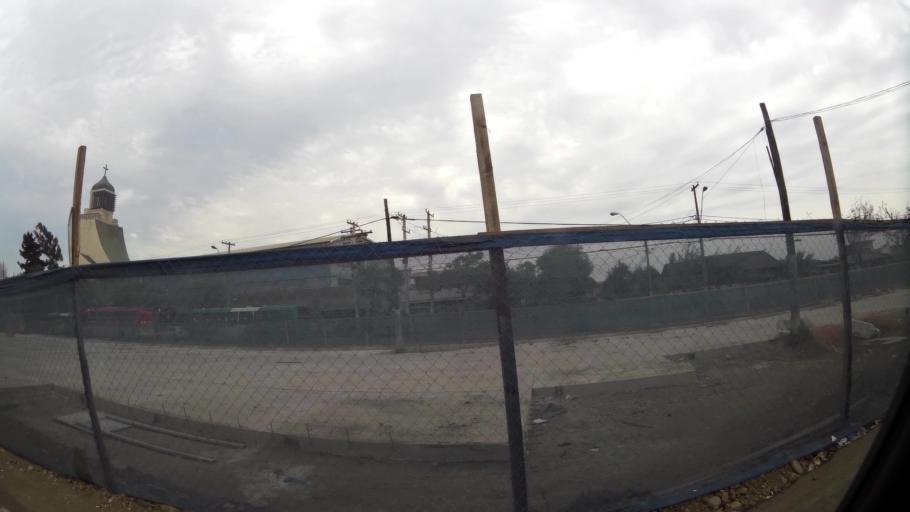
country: CL
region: Santiago Metropolitan
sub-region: Provincia de Santiago
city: Lo Prado
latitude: -33.5091
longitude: -70.7679
